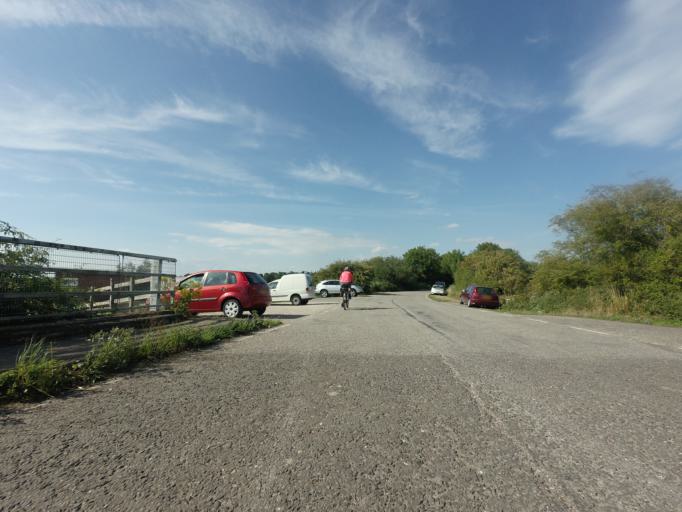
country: GB
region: England
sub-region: Kent
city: Tenterden
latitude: 51.0010
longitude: 0.6854
